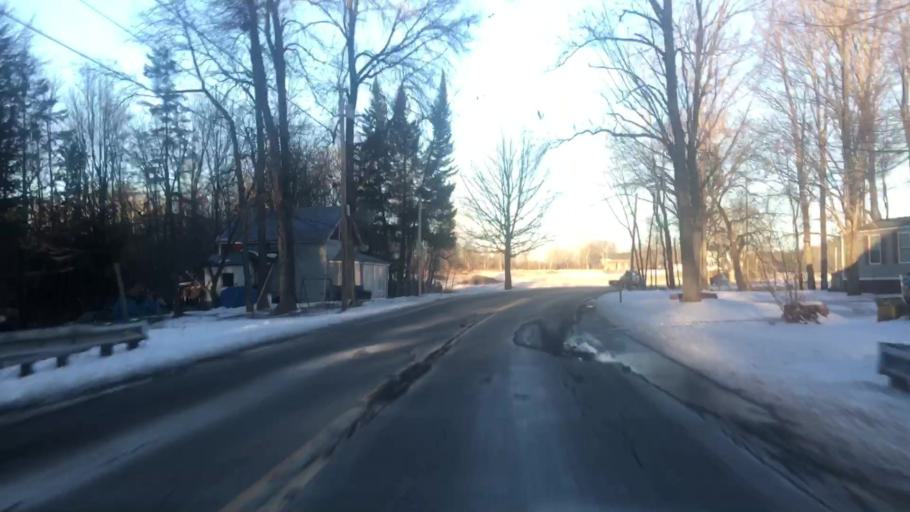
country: US
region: Maine
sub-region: Kennebec County
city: Benton
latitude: 44.5778
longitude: -69.5602
